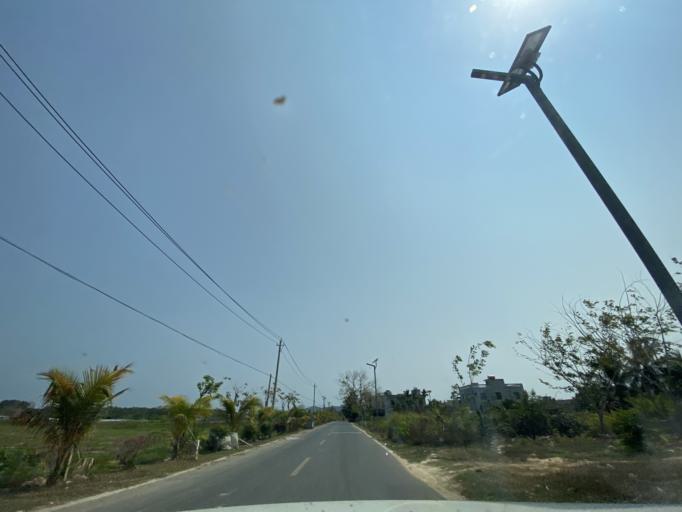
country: CN
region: Hainan
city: Yingzhou
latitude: 18.4164
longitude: 109.8143
